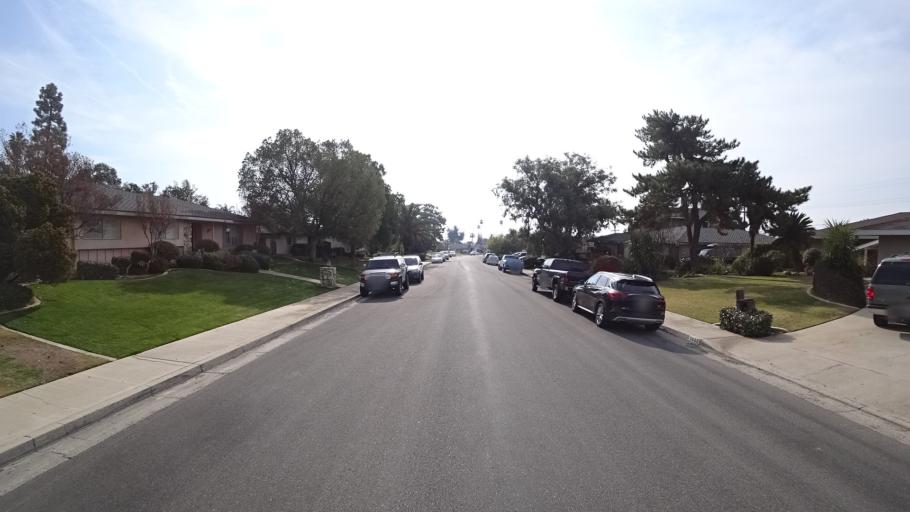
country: US
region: California
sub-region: Kern County
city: Oildale
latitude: 35.4034
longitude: -118.9518
